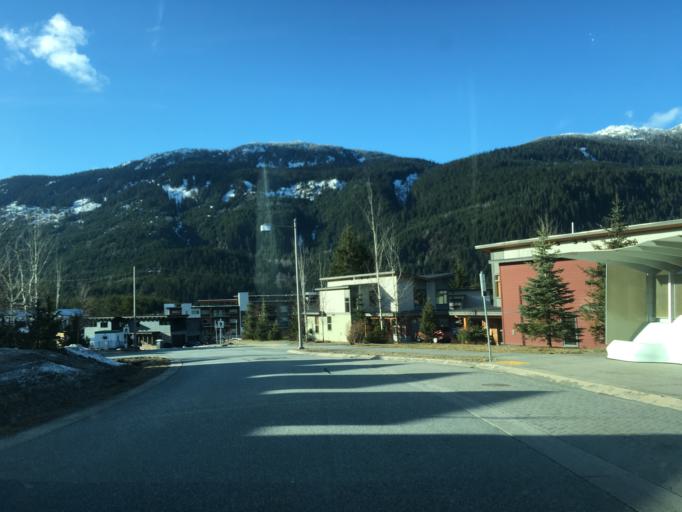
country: CA
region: British Columbia
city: Whistler
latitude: 50.0789
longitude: -123.0391
